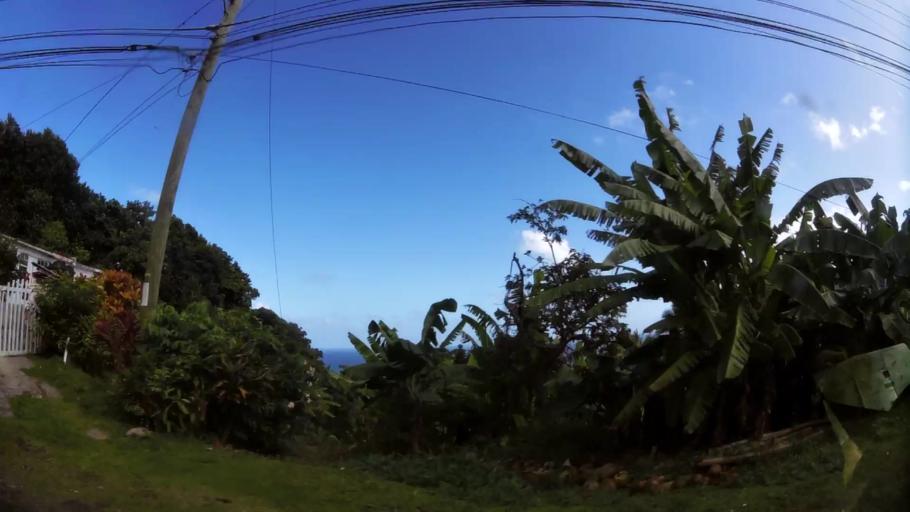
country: DM
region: Saint Andrew
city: Marigot
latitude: 15.5159
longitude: -61.2630
